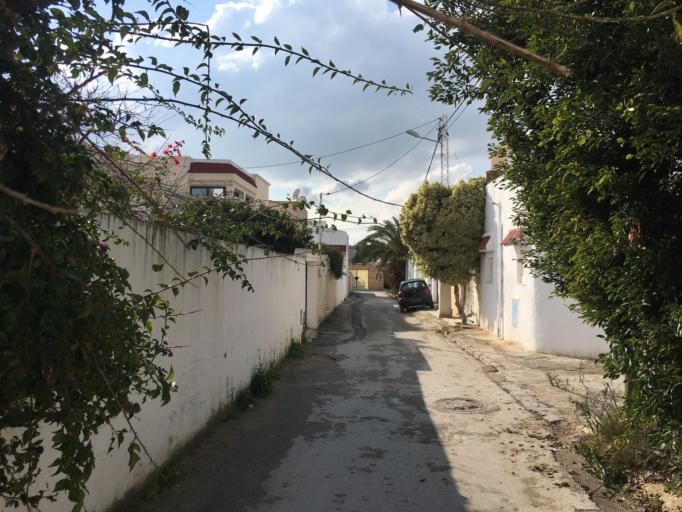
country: TN
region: Tunis
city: Al Marsa
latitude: 36.9040
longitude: 10.2930
